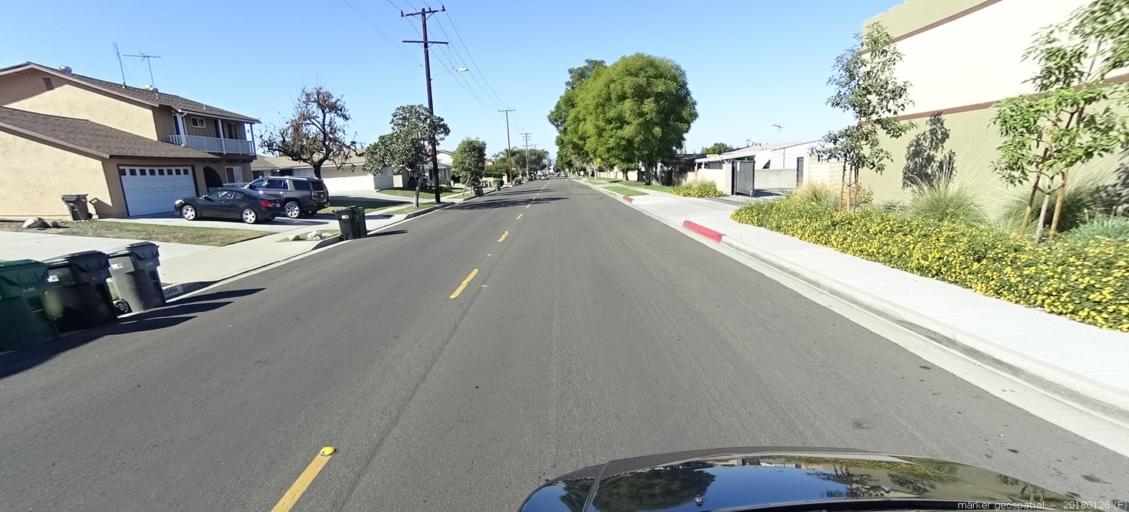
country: US
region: California
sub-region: Los Angeles County
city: Walnut
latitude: 34.0029
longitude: -117.8494
